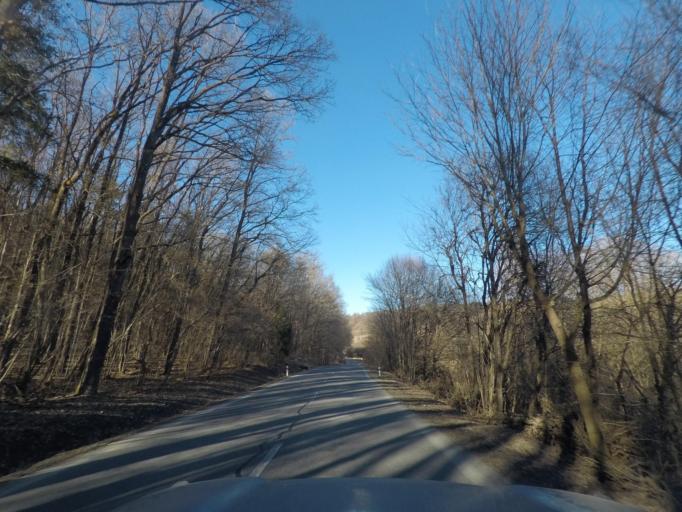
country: SK
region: Presovsky
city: Medzilaborce
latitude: 49.1674
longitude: 22.0218
